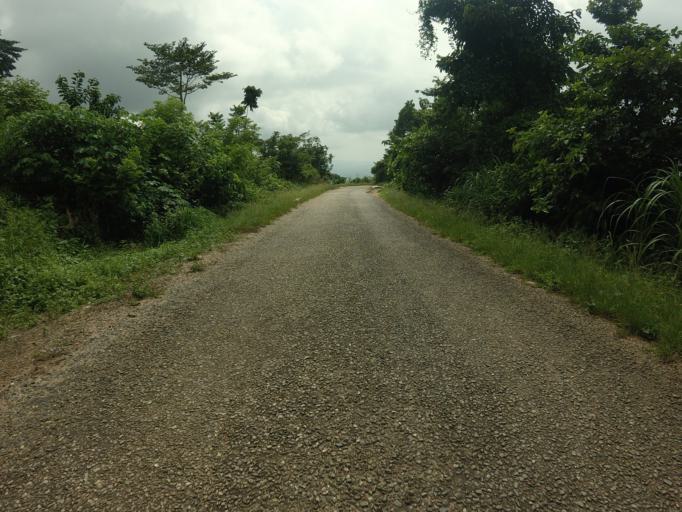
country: GH
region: Volta
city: Kpandu
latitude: 6.8446
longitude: 0.4327
